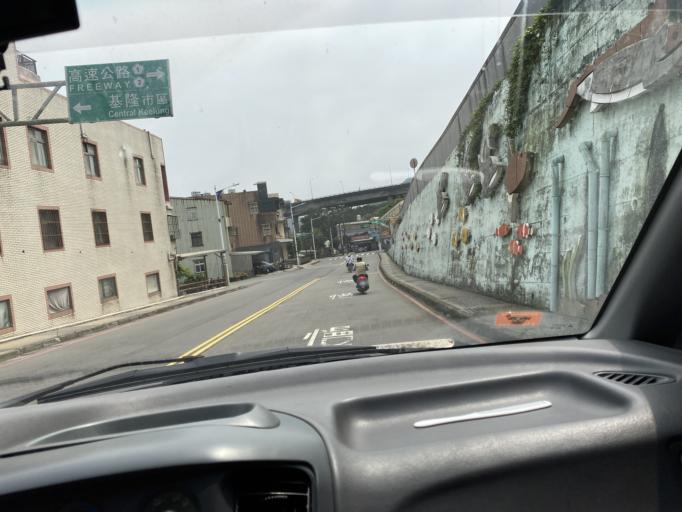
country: TW
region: Taiwan
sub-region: Keelung
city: Keelung
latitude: 25.1553
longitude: 121.7317
